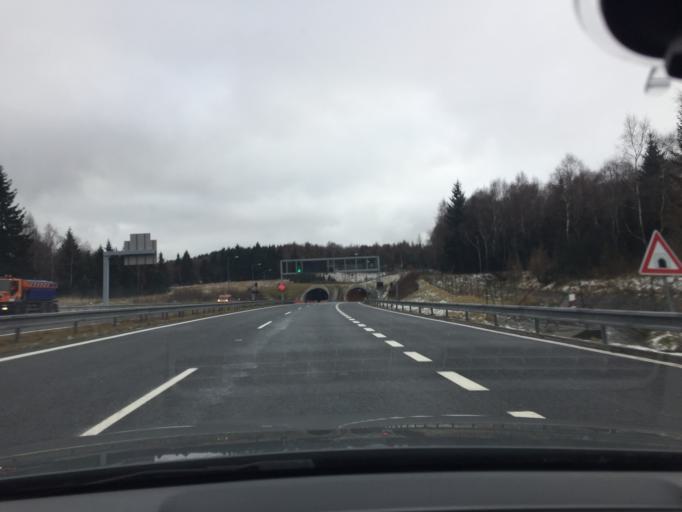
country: CZ
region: Ustecky
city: Chlumec
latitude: 50.7660
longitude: 13.9685
